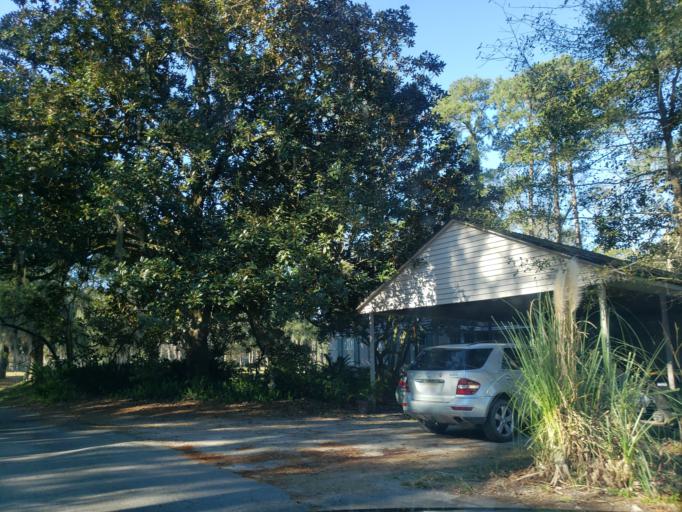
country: US
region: Georgia
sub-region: Chatham County
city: Thunderbolt
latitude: 32.0181
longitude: -81.0914
